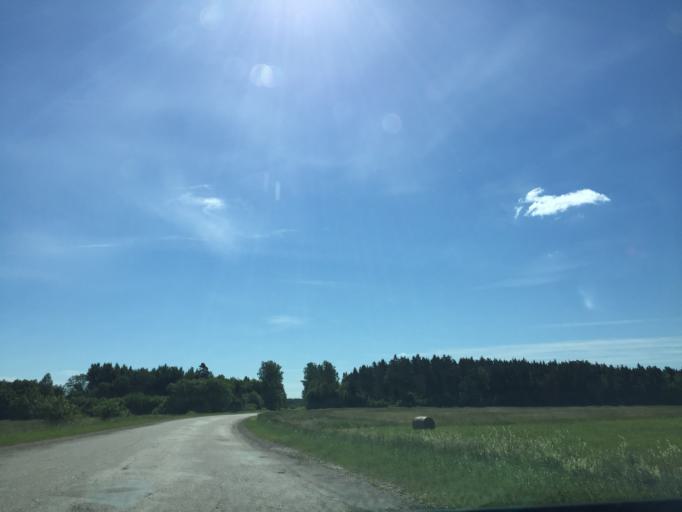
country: LV
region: Dundaga
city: Dundaga
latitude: 57.3612
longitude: 22.0381
